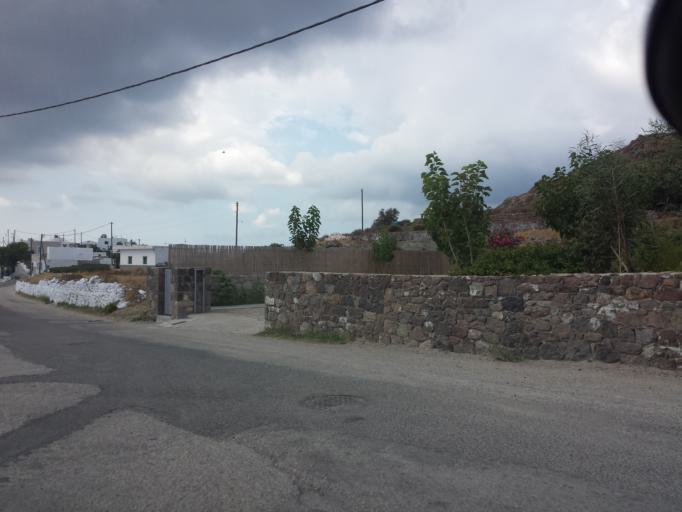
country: GR
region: South Aegean
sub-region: Nomos Kykladon
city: Milos
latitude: 36.7423
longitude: 24.4244
